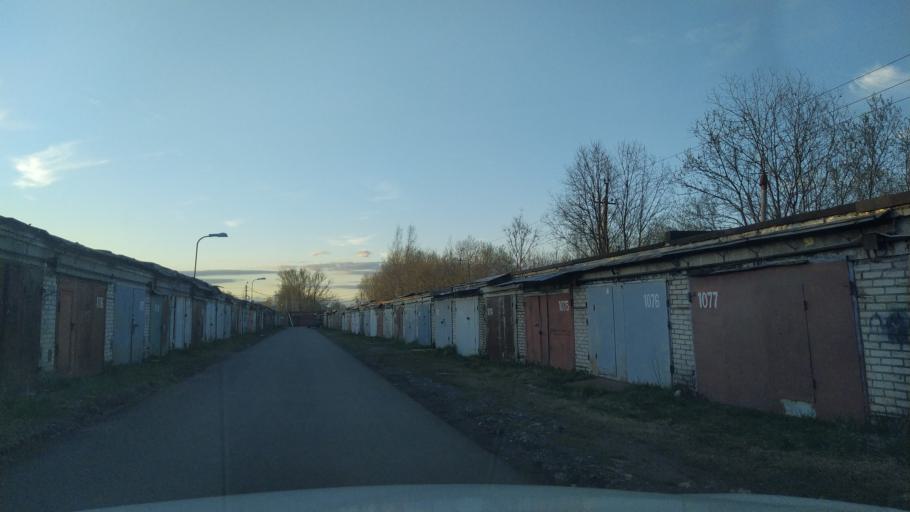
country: RU
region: St.-Petersburg
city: Pushkin
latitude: 59.6918
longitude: 30.3961
